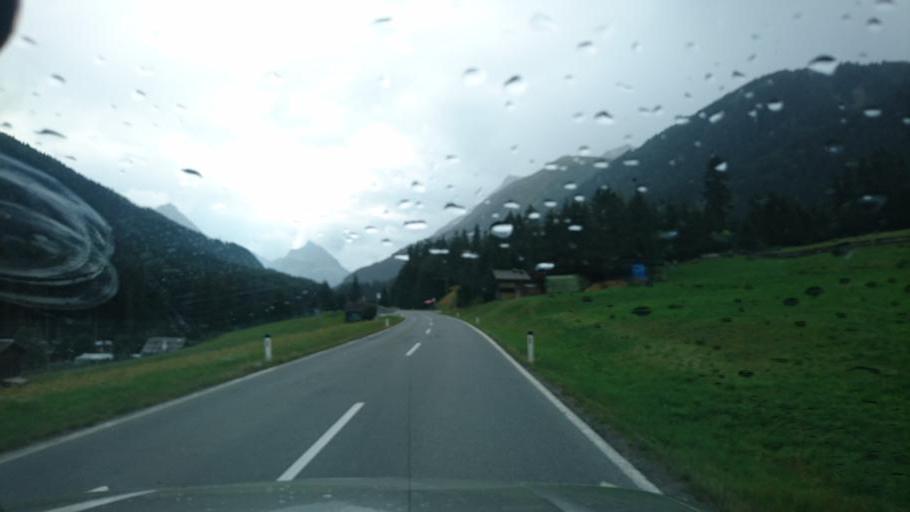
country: AT
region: Tyrol
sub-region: Politischer Bezirk Landeck
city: Galtur
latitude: 46.9857
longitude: 10.2381
